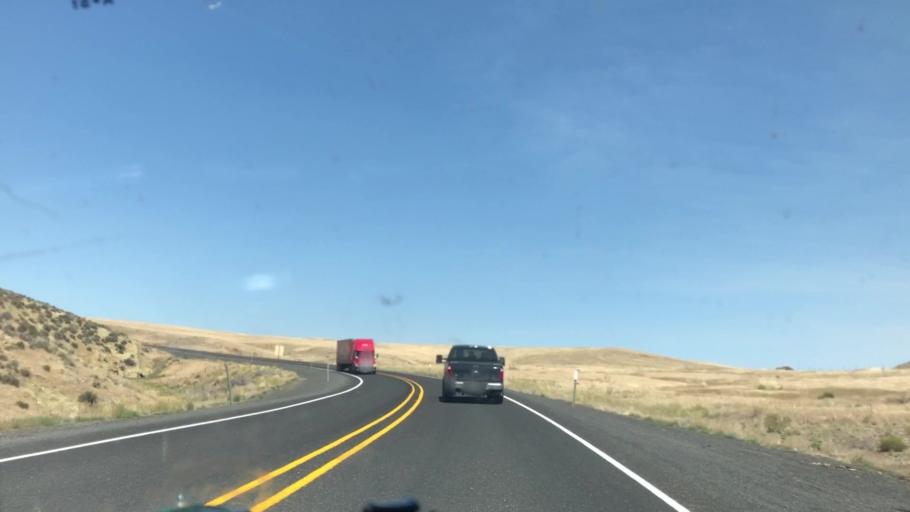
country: US
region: Idaho
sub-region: Owyhee County
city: Marsing
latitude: 43.2309
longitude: -117.0483
